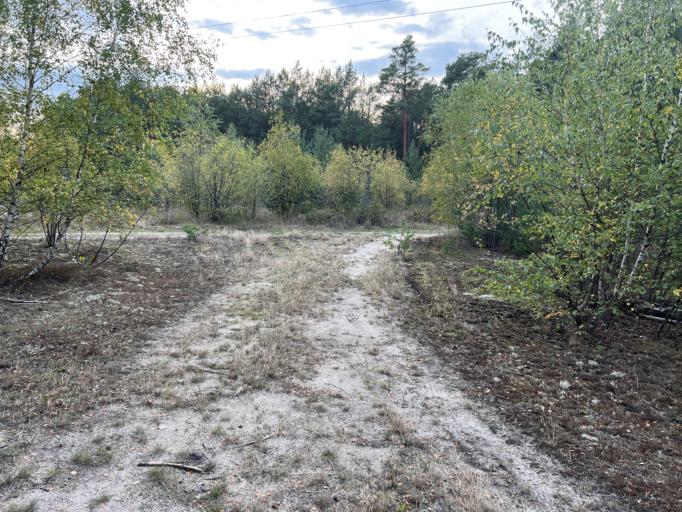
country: DE
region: Brandenburg
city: Teupitz
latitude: 52.1092
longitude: 13.6348
